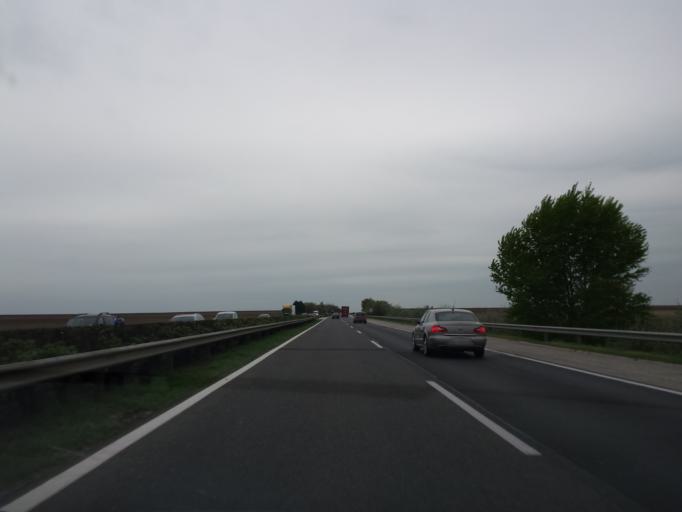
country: HU
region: Pest
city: Zsambek
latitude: 47.5083
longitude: 18.6980
